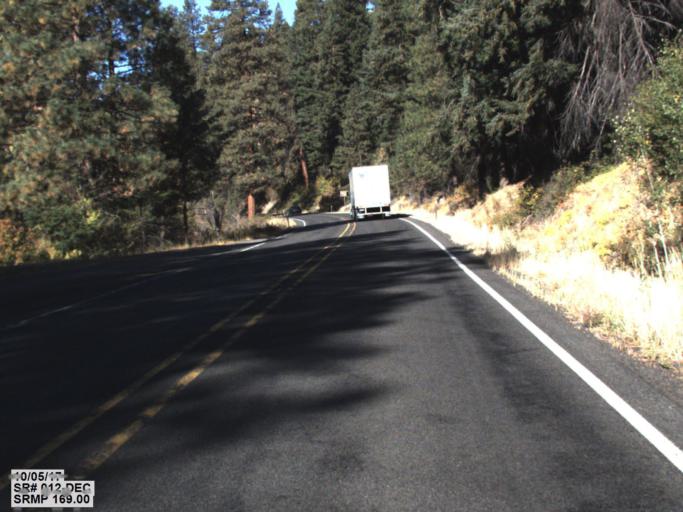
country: US
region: Washington
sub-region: Yakima County
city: Tieton
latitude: 46.6765
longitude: -121.0660
